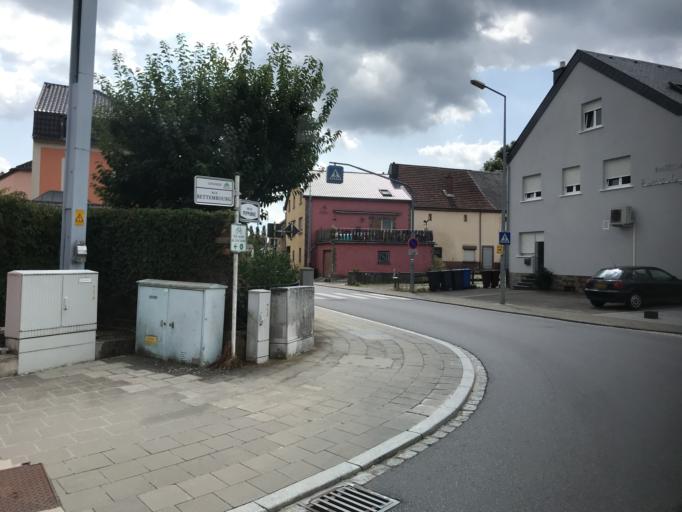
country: LU
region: Luxembourg
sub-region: Canton d'Esch-sur-Alzette
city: Bettembourg
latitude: 49.5297
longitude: 6.1189
